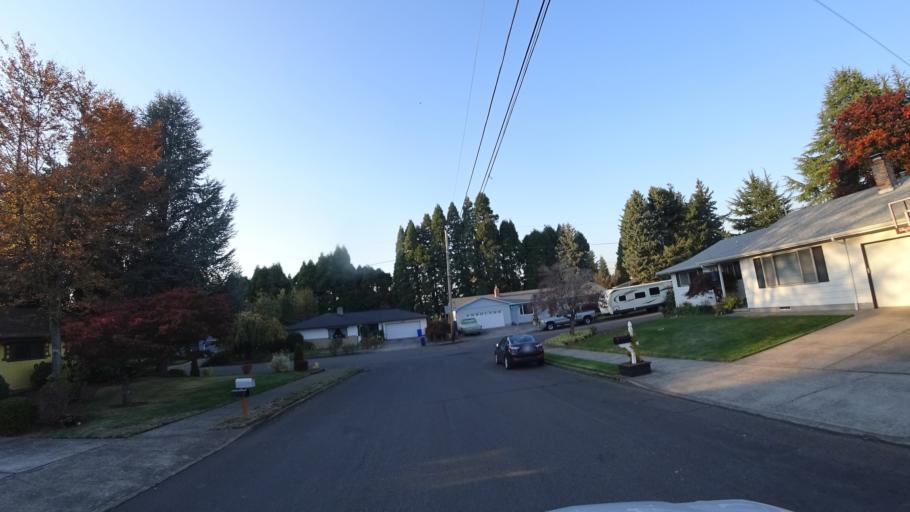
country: US
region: Oregon
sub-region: Multnomah County
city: Gresham
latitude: 45.5173
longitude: -122.4427
